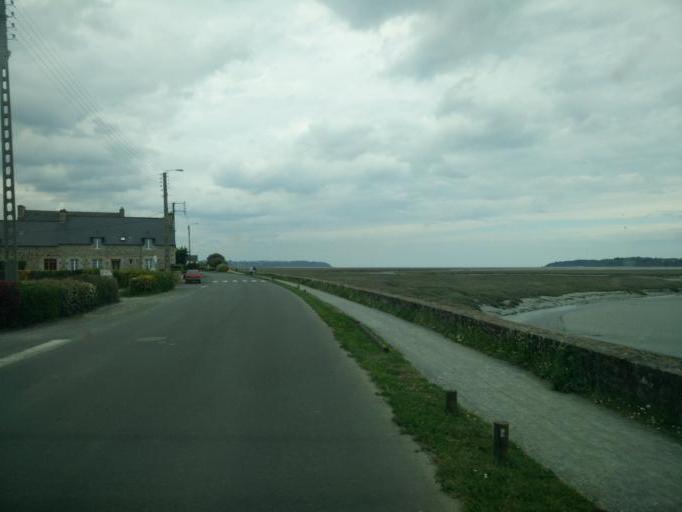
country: FR
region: Brittany
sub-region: Departement des Cotes-d'Armor
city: Yffiniac
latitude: 48.4951
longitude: -2.6874
